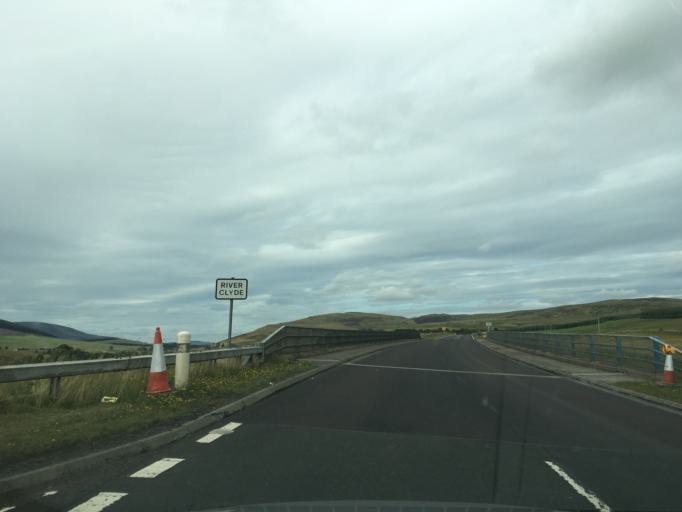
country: GB
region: Scotland
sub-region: South Lanarkshire
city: Douglas
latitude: 55.5221
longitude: -3.6799
